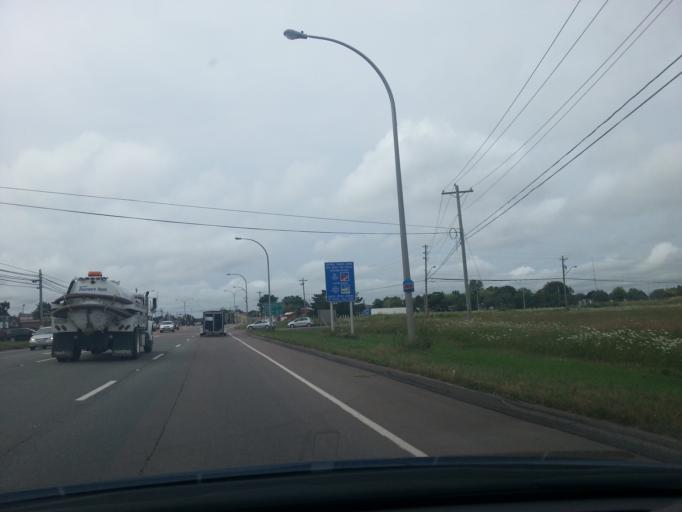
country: CA
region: Prince Edward Island
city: Charlottetown
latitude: 46.2708
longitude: -63.1115
